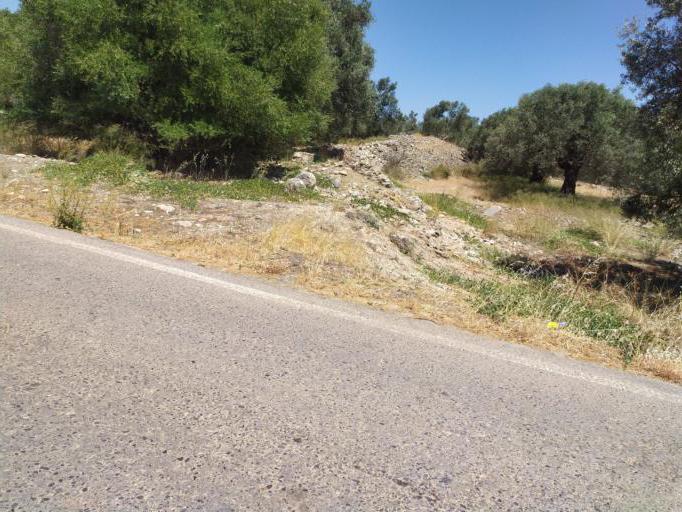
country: GR
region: Crete
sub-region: Nomos Irakleiou
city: Agioi Deka
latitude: 35.0609
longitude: 24.9477
